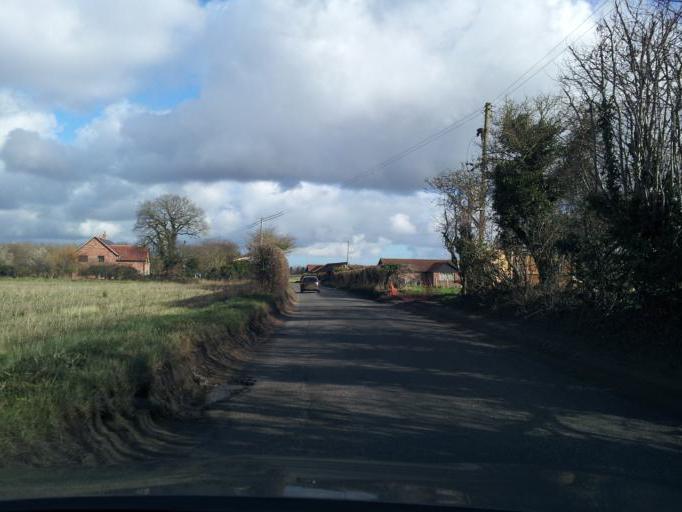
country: GB
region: England
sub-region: Norfolk
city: Mattishall
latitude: 52.6590
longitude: 1.0560
